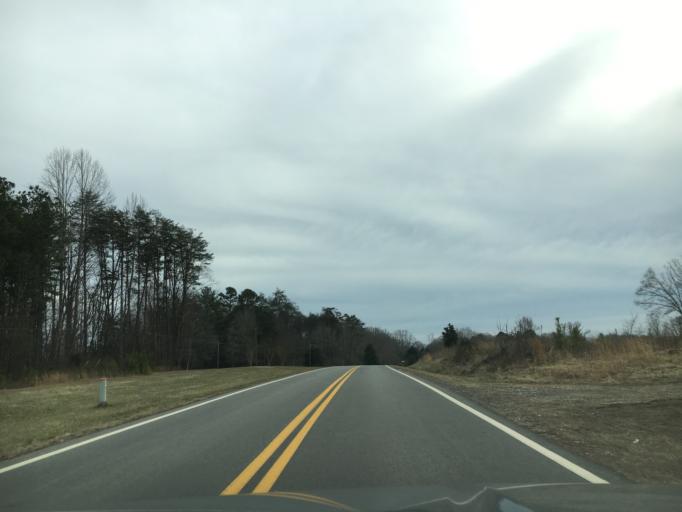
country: US
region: Virginia
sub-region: Charlotte County
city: Charlotte Court House
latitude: 37.0927
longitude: -78.7453
